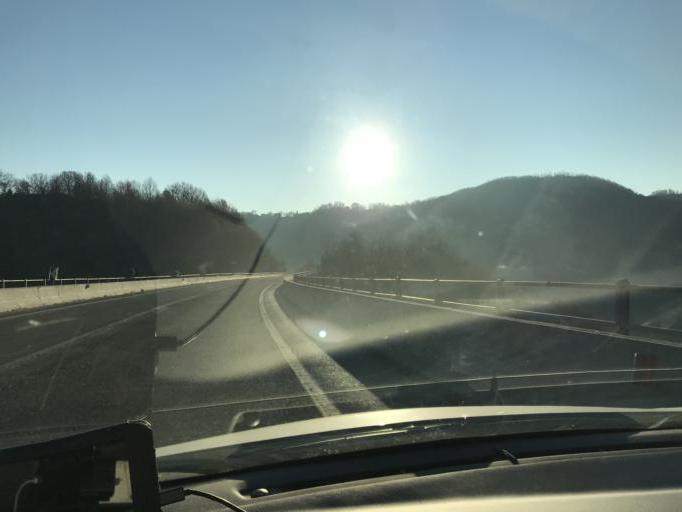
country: IT
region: Latium
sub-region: Provincia di Rieti
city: Fiamignano
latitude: 42.2567
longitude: 13.1347
